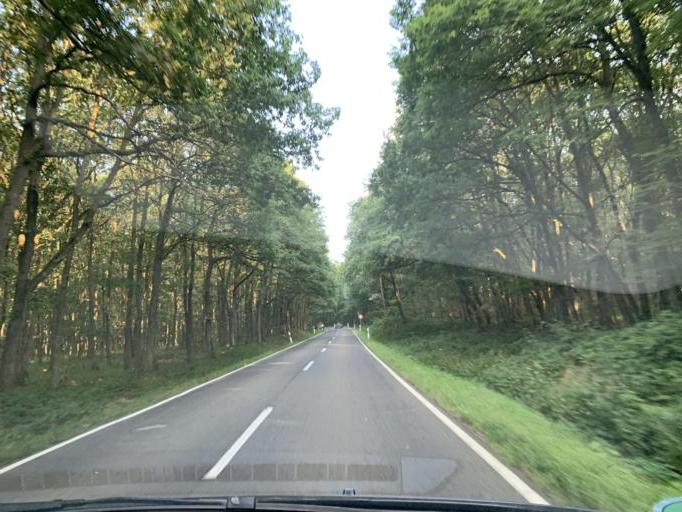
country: DE
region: North Rhine-Westphalia
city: Heimbach
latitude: 50.6515
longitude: 6.4457
